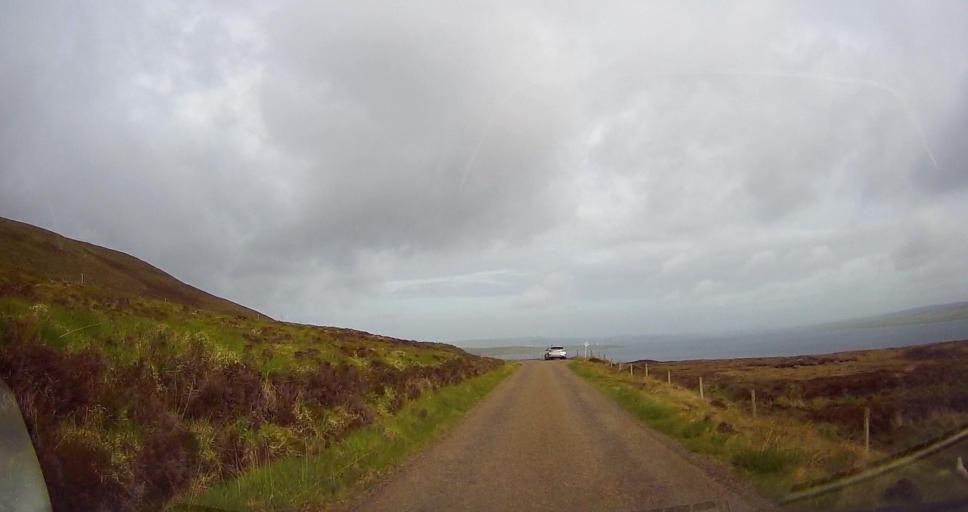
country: GB
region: Scotland
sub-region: Orkney Islands
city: Stromness
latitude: 58.8846
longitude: -3.2497
